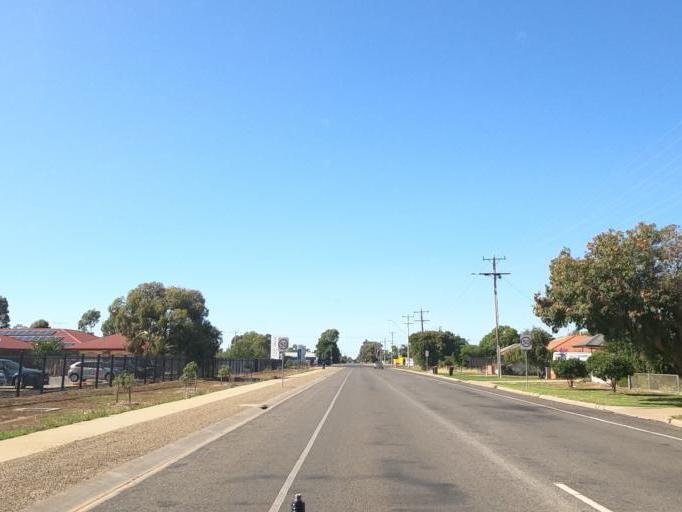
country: AU
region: Victoria
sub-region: Moira
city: Yarrawonga
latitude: -36.0134
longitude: 146.0132
